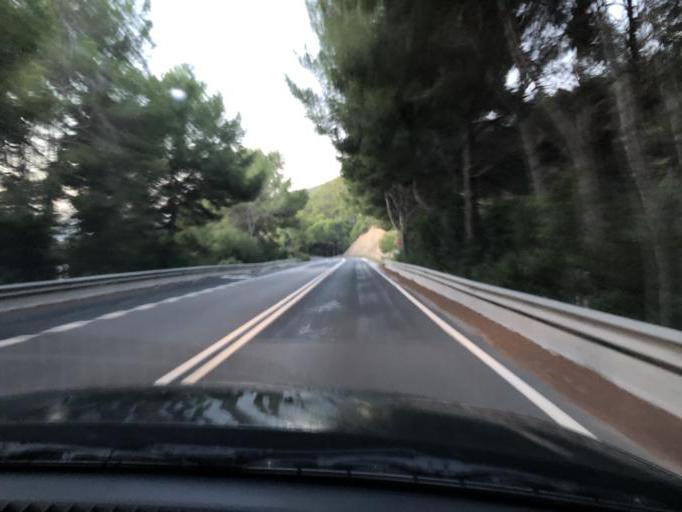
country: ES
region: Balearic Islands
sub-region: Illes Balears
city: Andratx
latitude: 39.5600
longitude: 2.4214
